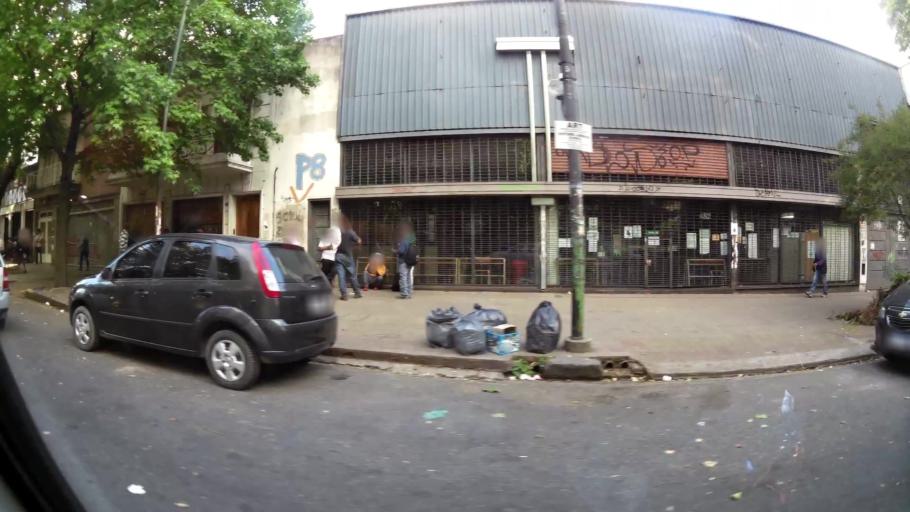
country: AR
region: Buenos Aires
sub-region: Partido de La Plata
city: La Plata
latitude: -34.9084
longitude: -57.9528
